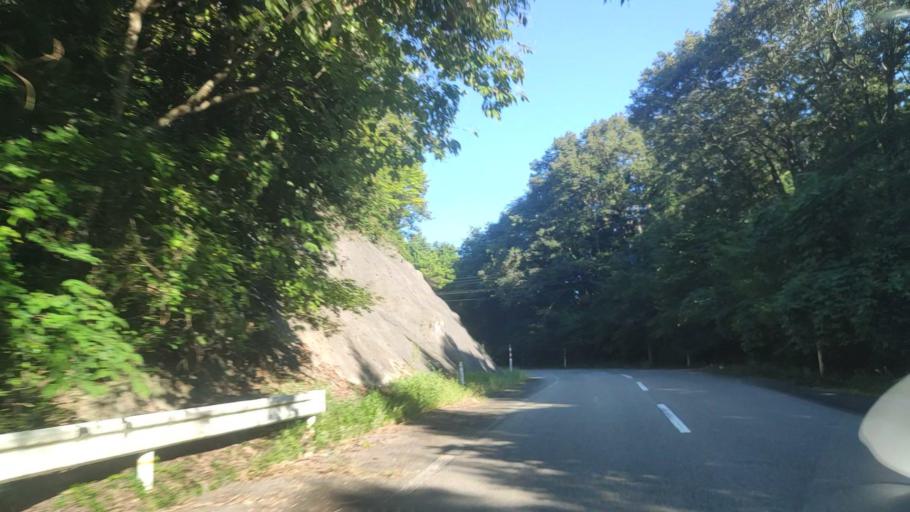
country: JP
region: Ishikawa
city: Nanao
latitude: 37.1121
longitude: 136.9623
